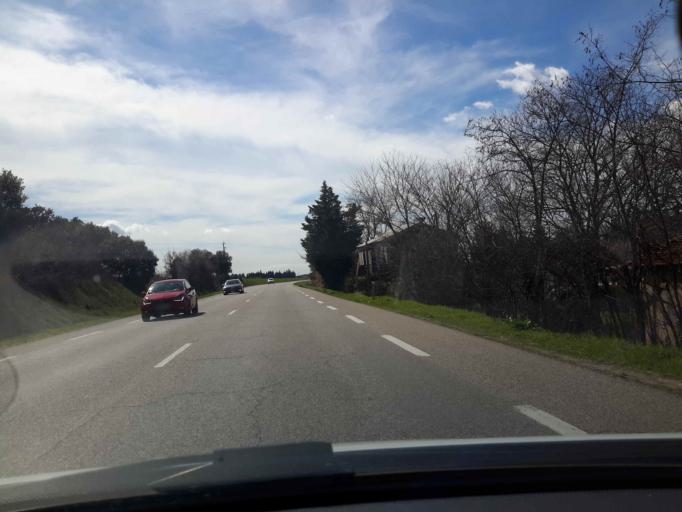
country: FR
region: Languedoc-Roussillon
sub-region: Departement du Gard
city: Aubord
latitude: 43.7456
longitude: 4.3000
